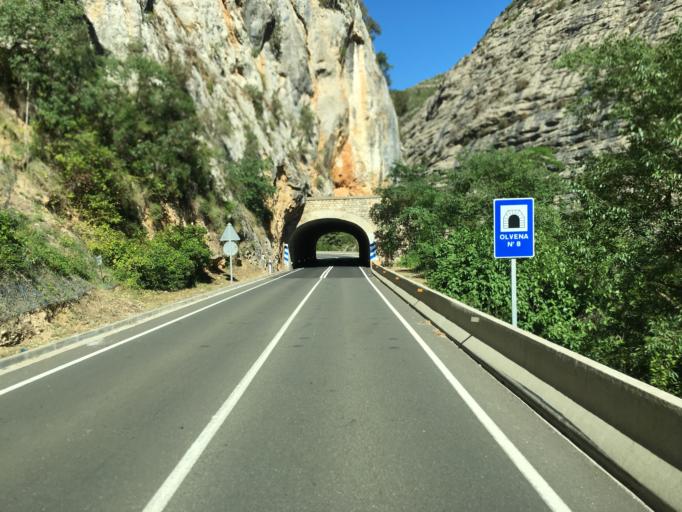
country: ES
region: Aragon
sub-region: Provincia de Huesca
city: Estada
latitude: 42.1048
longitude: 0.2867
